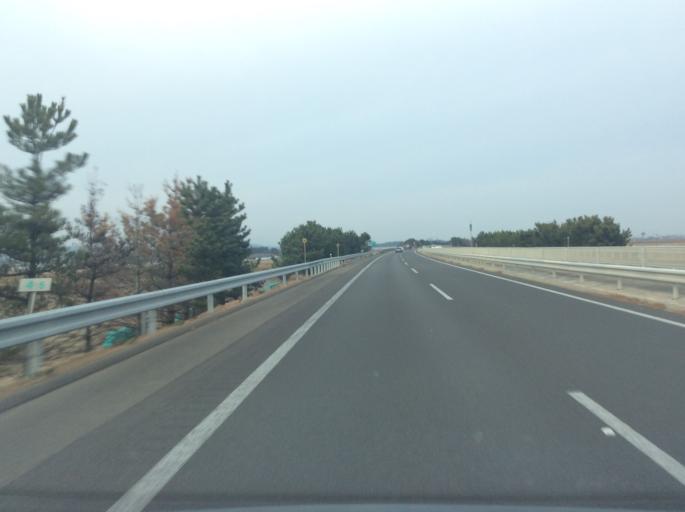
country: JP
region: Miyagi
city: Iwanuma
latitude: 38.1156
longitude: 140.8877
